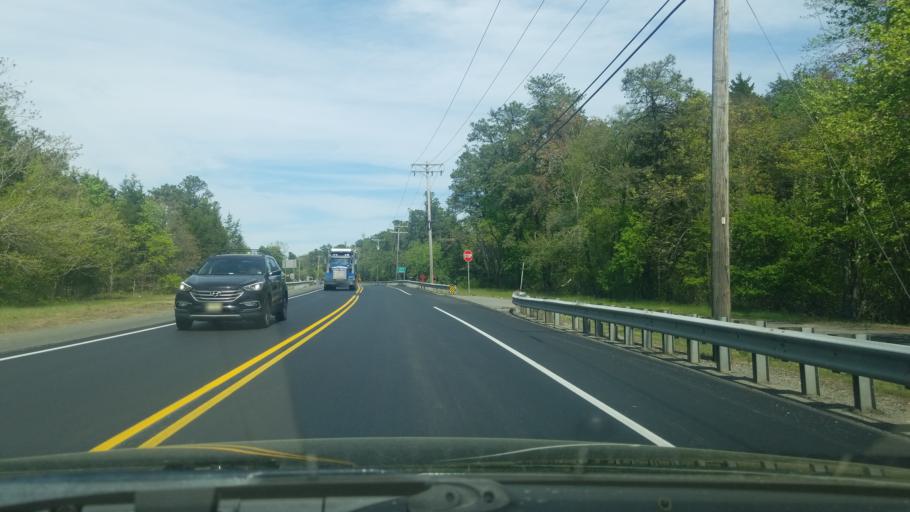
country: US
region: New Jersey
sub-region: Ocean County
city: Lakehurst
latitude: 40.0080
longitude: -74.3309
